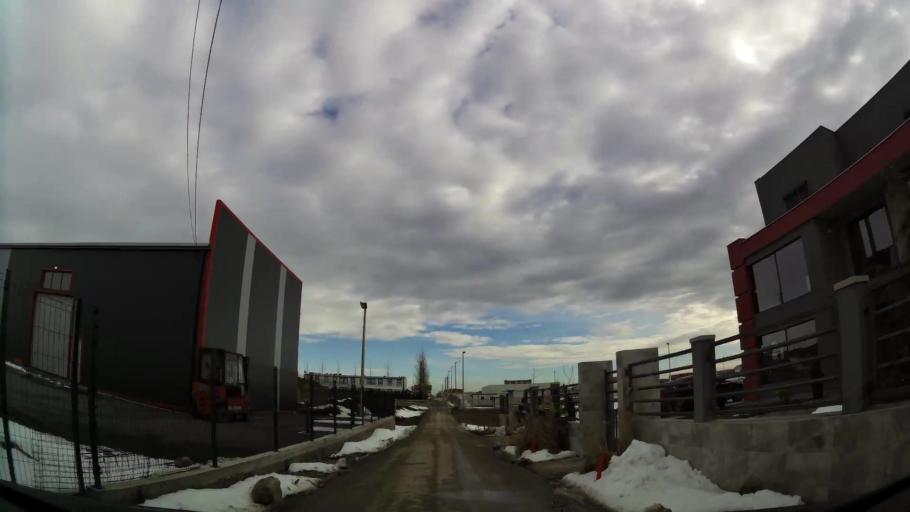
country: RS
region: Central Serbia
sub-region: Belgrade
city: Surcin
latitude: 44.8011
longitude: 20.3122
